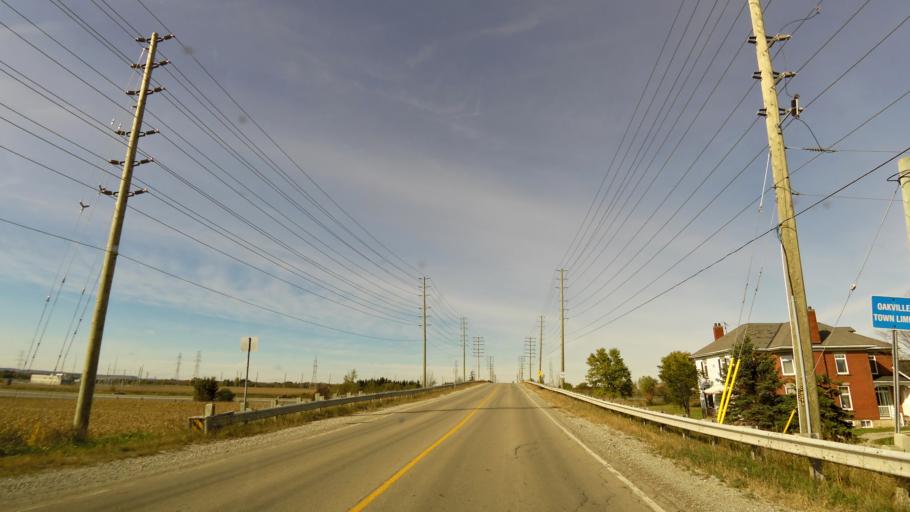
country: CA
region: Ontario
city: Oakville
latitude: 43.4987
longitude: -79.7554
